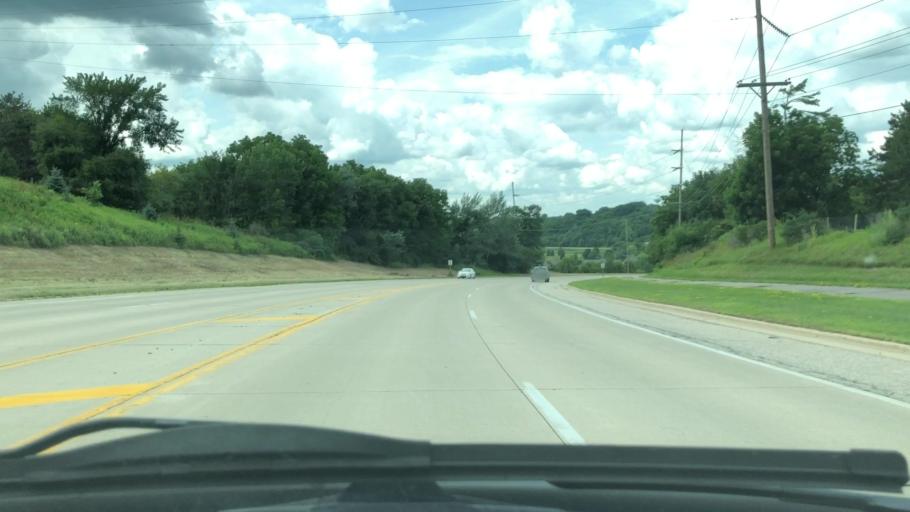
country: US
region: Minnesota
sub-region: Olmsted County
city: Rochester
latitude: 44.0136
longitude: -92.5150
